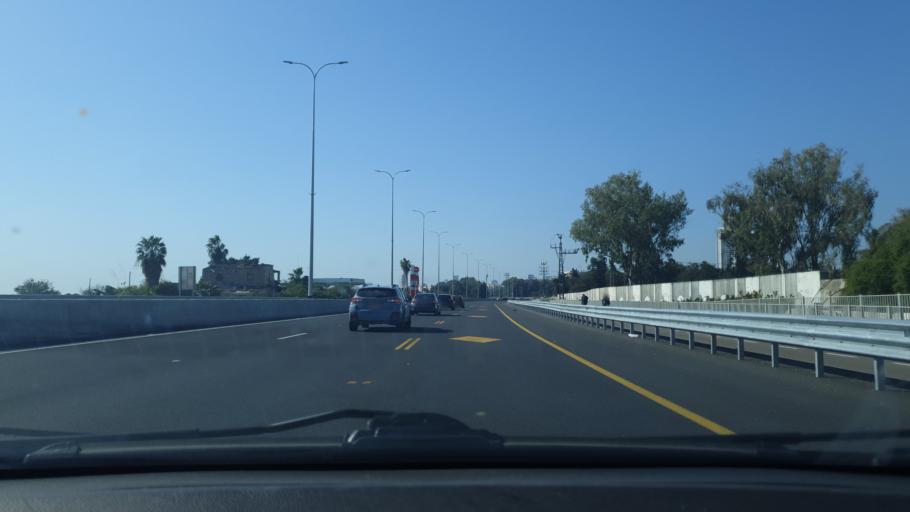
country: IL
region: Tel Aviv
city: Azor
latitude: 32.0393
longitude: 34.8252
